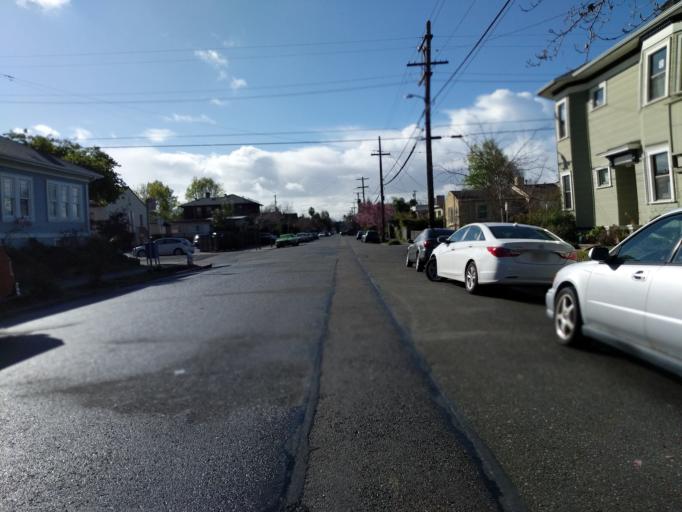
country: US
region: California
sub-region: Alameda County
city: Berkeley
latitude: 37.8605
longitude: -122.2761
